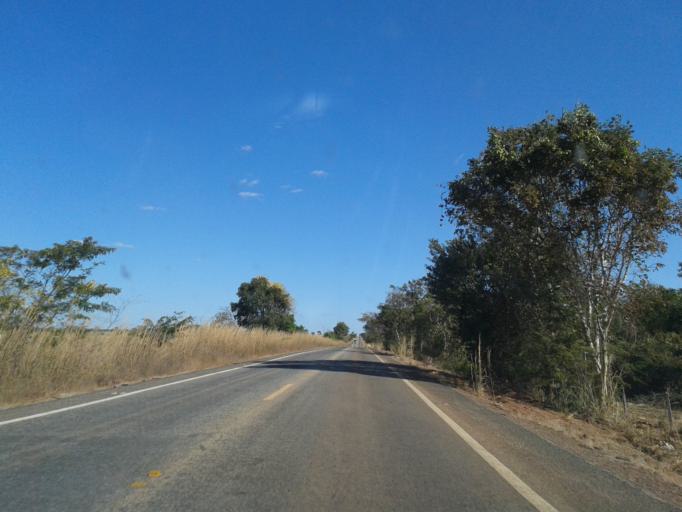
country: BR
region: Goias
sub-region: Mozarlandia
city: Mozarlandia
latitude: -14.5038
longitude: -50.4848
